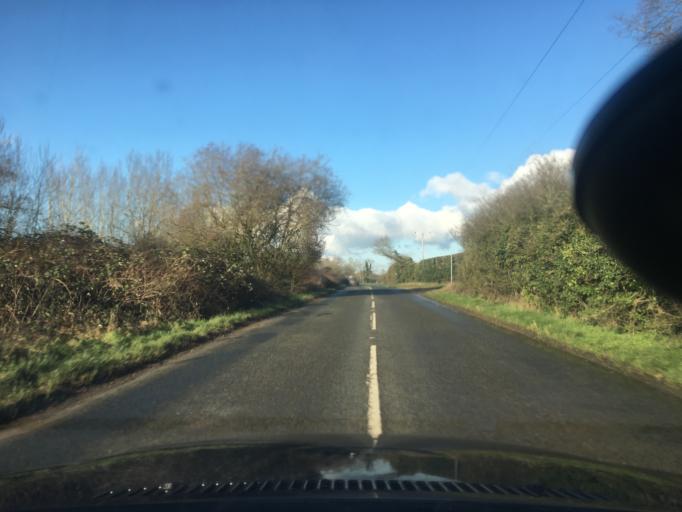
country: GB
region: England
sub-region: West Berkshire
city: Stratfield Mortimer
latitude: 51.3840
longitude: -1.0212
